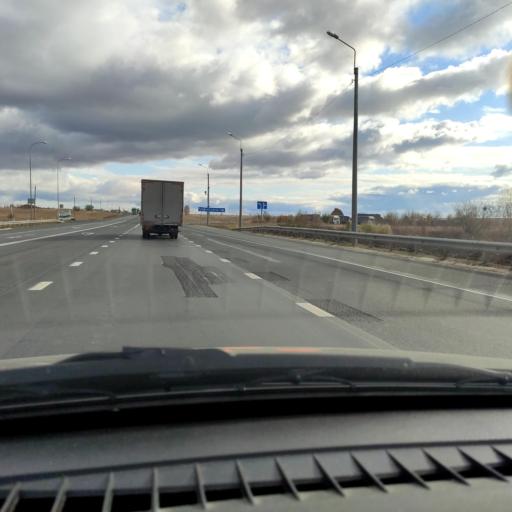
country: RU
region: Samara
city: Syzran'
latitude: 53.2105
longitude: 48.4858
